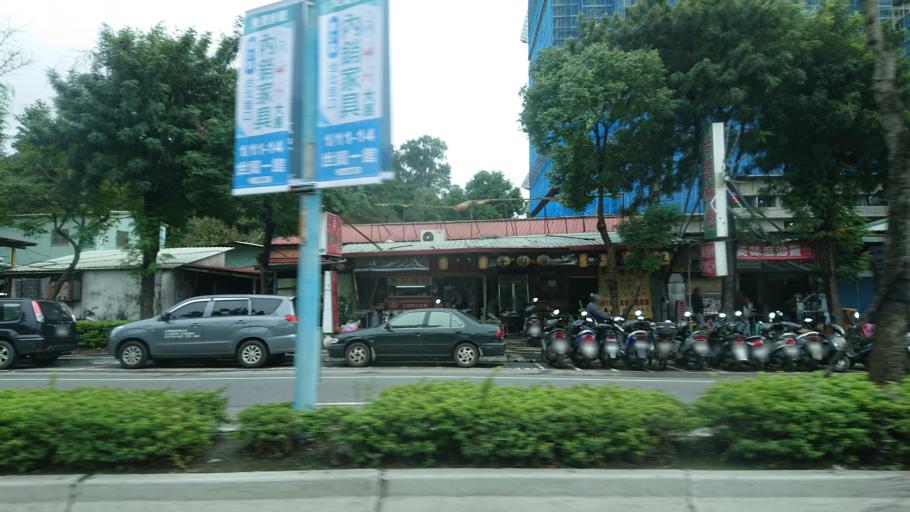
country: TW
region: Taipei
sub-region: Taipei
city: Banqiao
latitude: 24.9772
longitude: 121.4490
